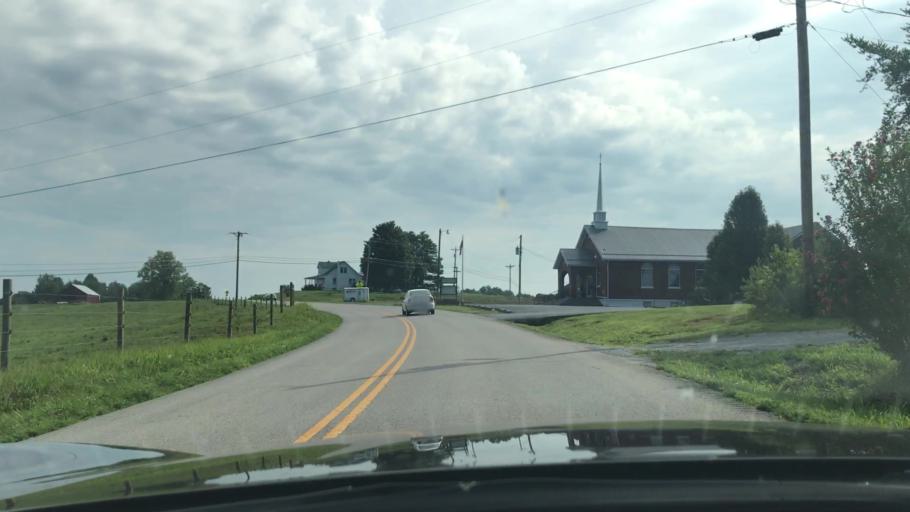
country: US
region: Kentucky
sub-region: Green County
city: Greensburg
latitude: 37.2639
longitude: -85.5461
